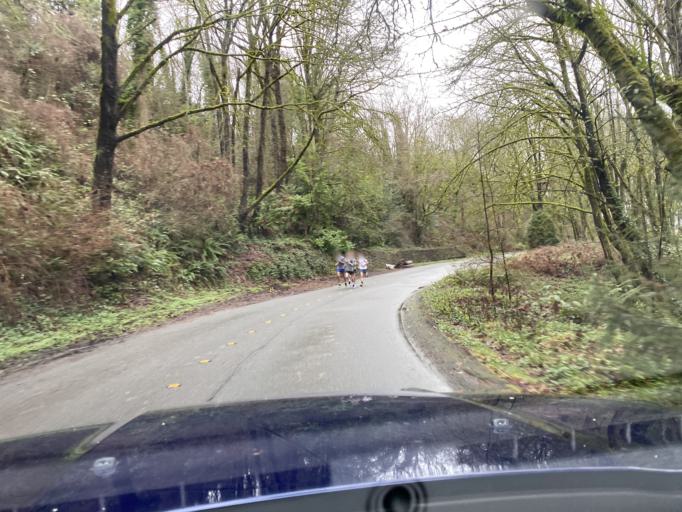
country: US
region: Washington
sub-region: King County
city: Seattle
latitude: 47.6367
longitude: -122.3107
